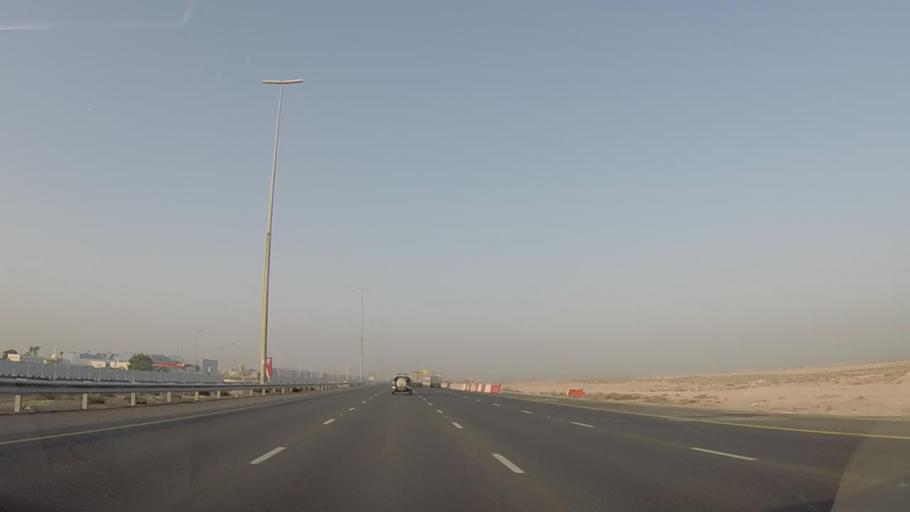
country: AE
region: Dubai
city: Dubai
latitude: 24.9283
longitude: 55.0078
